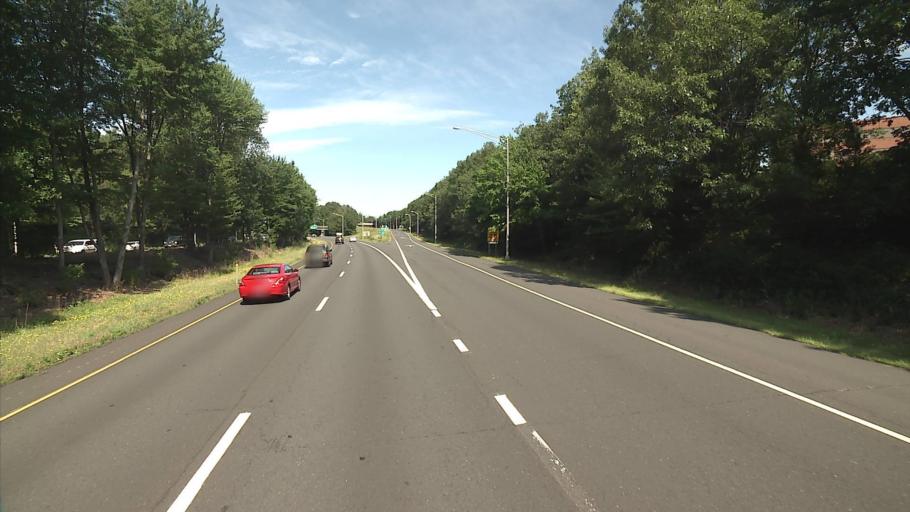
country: US
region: Connecticut
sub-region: Hartford County
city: Glastonbury Center
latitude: 41.7119
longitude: -72.5876
